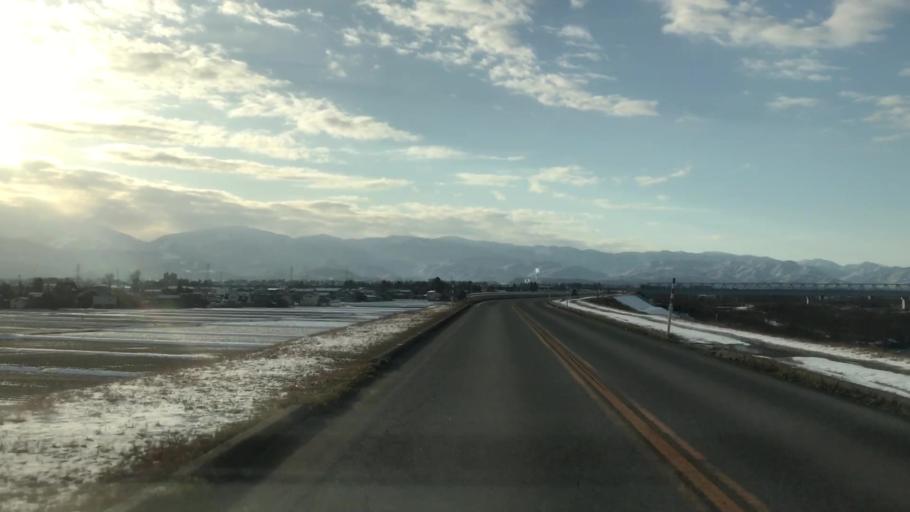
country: JP
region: Toyama
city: Toyama-shi
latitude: 36.6784
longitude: 137.2848
